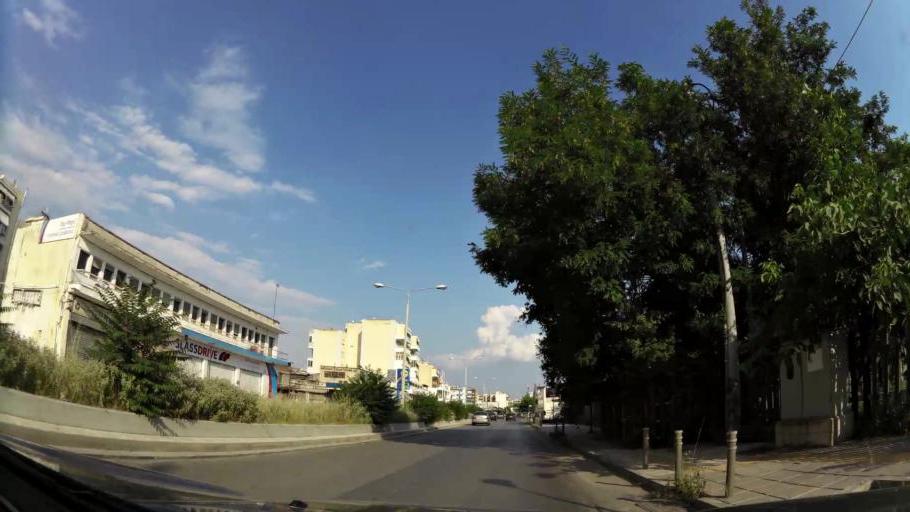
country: GR
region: Central Macedonia
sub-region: Nomos Thessalonikis
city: Menemeni
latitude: 40.6663
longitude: 22.8923
